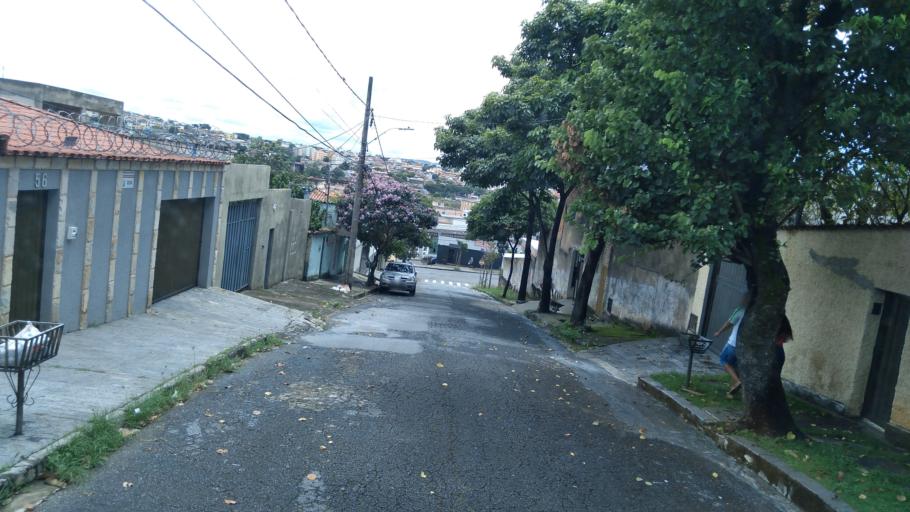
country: BR
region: Minas Gerais
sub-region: Belo Horizonte
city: Belo Horizonte
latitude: -19.8560
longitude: -43.9166
